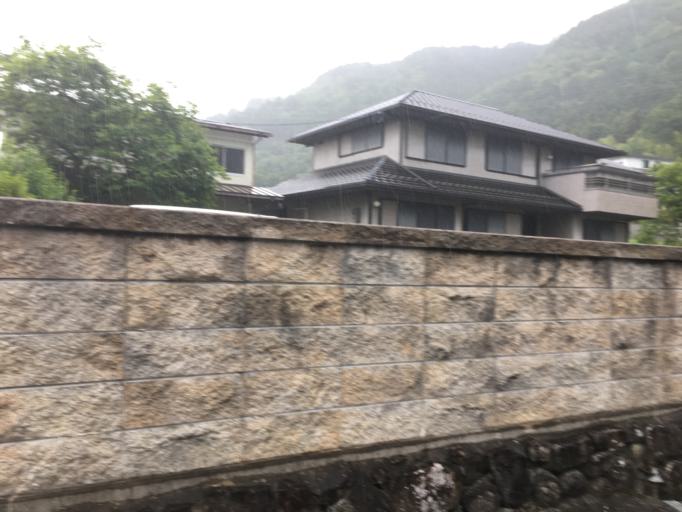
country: JP
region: Kyoto
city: Kameoka
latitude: 35.0104
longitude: 135.6115
